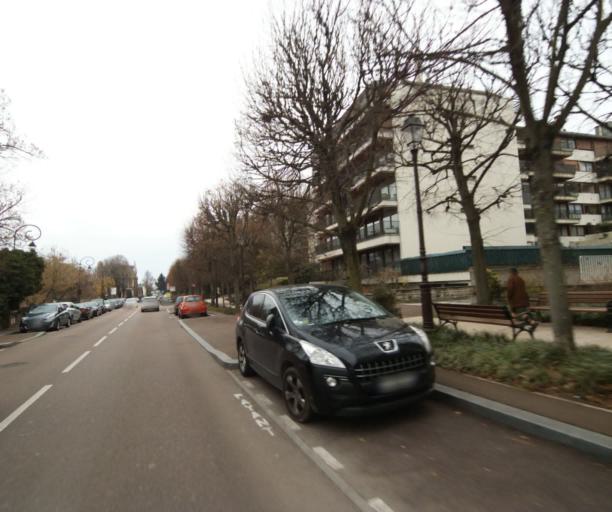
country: FR
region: Ile-de-France
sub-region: Departement des Hauts-de-Seine
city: Saint-Cloud
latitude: 48.8529
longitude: 2.2160
